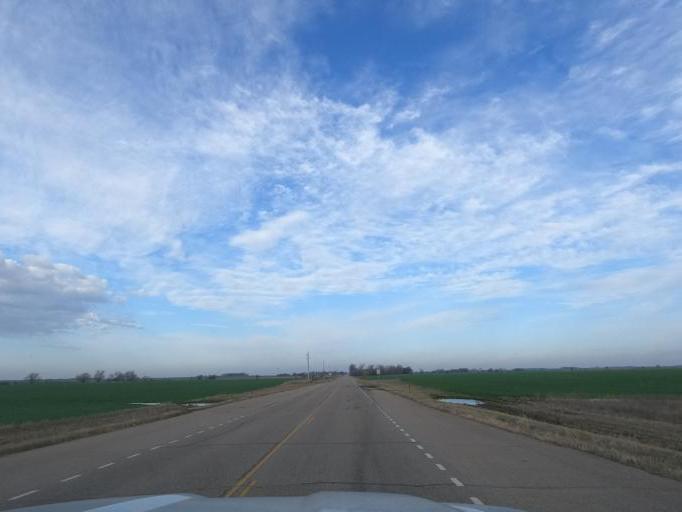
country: US
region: Kansas
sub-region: Reno County
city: Nickerson
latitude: 38.0578
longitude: -98.1798
